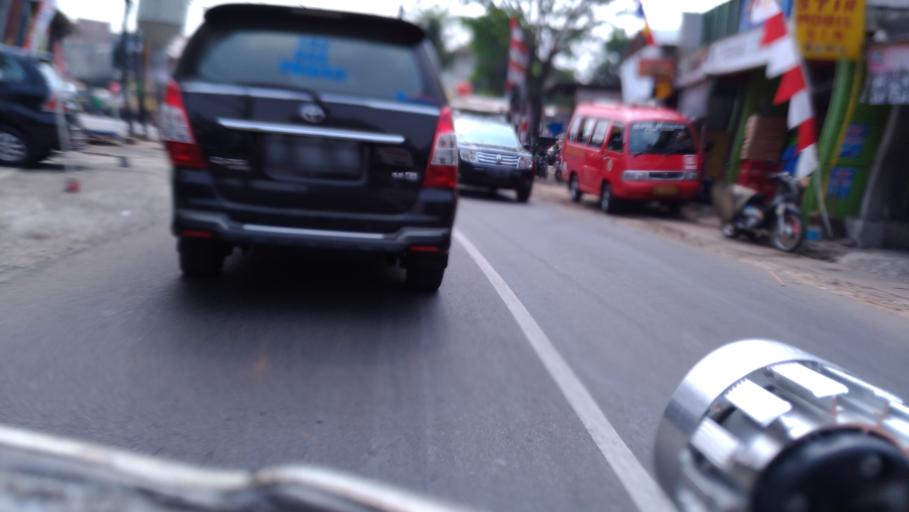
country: ID
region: West Java
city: Cileungsir
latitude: -6.3148
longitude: 106.8938
